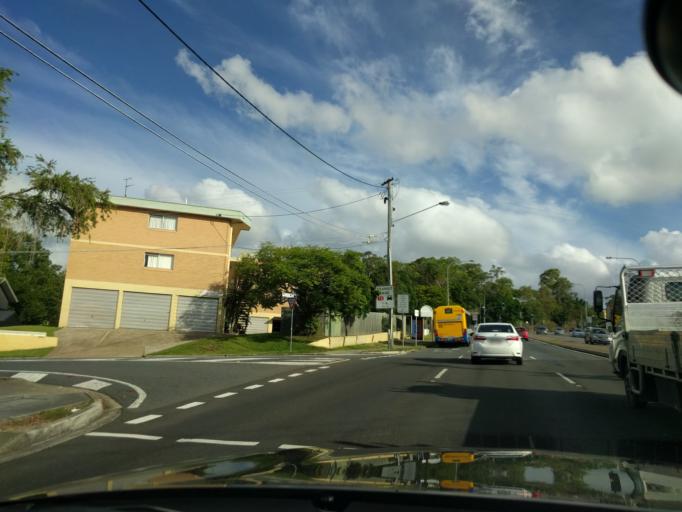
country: AU
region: Queensland
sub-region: Brisbane
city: Wilston
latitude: -27.4479
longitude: 153.0103
